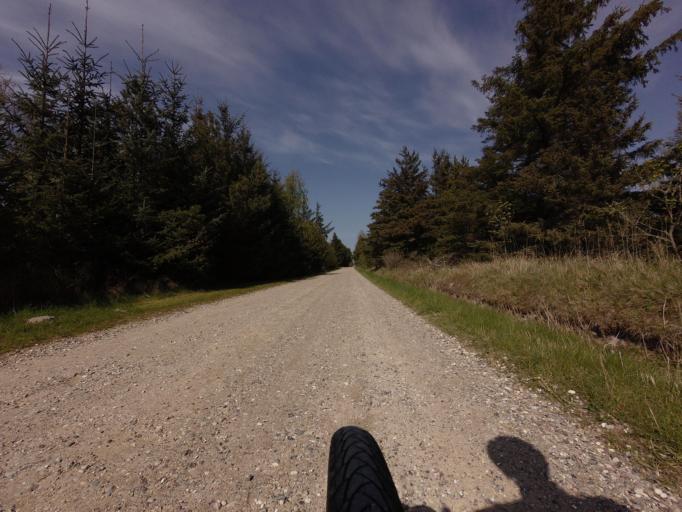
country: DK
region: North Denmark
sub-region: Jammerbugt Kommune
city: Brovst
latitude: 57.2047
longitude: 9.5510
